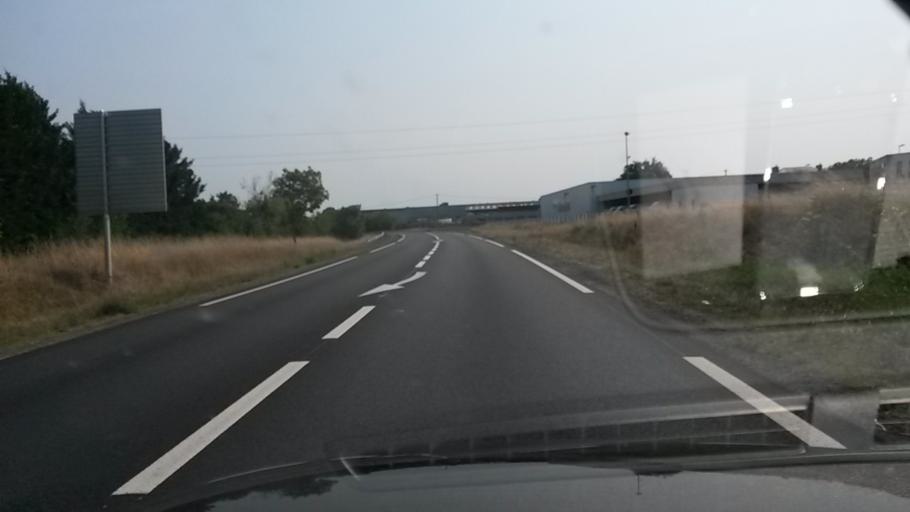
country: FR
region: Pays de la Loire
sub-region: Departement de la Loire-Atlantique
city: Ancenis
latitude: 47.3808
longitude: -1.1727
